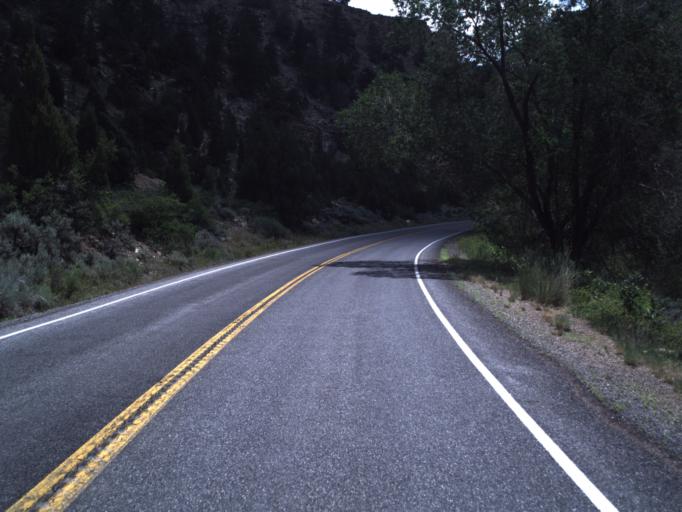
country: US
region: Utah
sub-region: Emery County
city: Huntington
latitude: 39.4124
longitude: -111.1149
